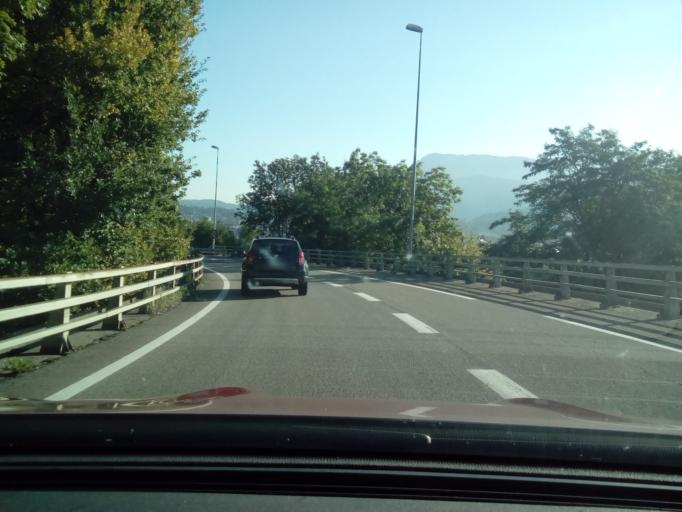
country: FR
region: Rhone-Alpes
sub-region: Departement de la Haute-Savoie
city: Cran-Gevrier
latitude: 45.8985
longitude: 6.1066
